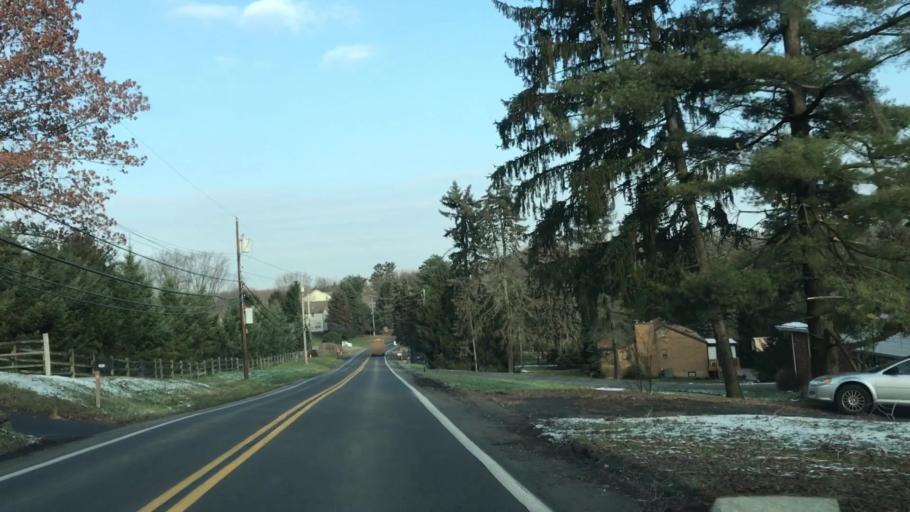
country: US
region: Pennsylvania
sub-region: Allegheny County
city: Franklin Park
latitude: 40.5612
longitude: -80.0776
